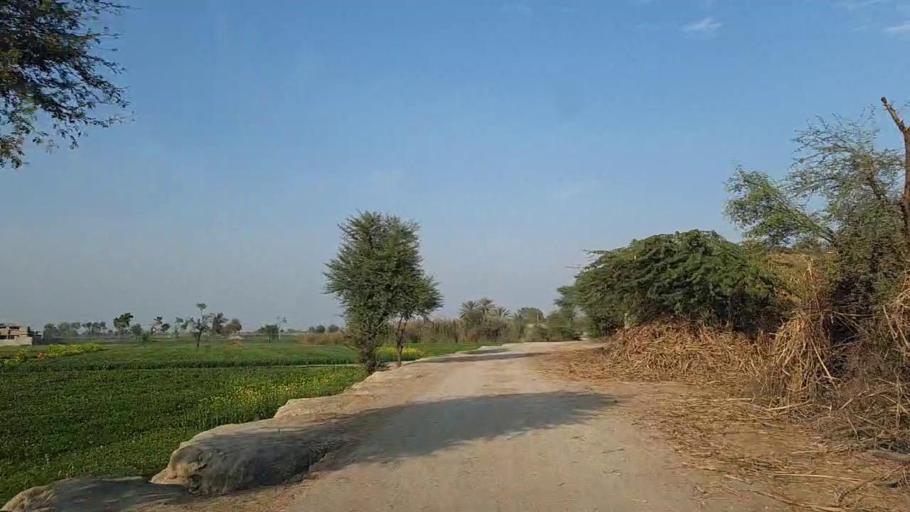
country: PK
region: Sindh
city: Nawabshah
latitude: 26.3723
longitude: 68.4941
